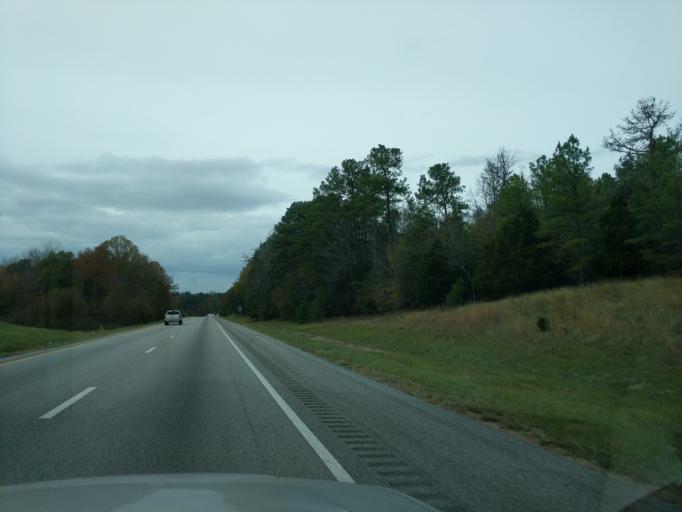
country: US
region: South Carolina
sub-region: Laurens County
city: Clinton
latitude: 34.5125
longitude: -81.8673
